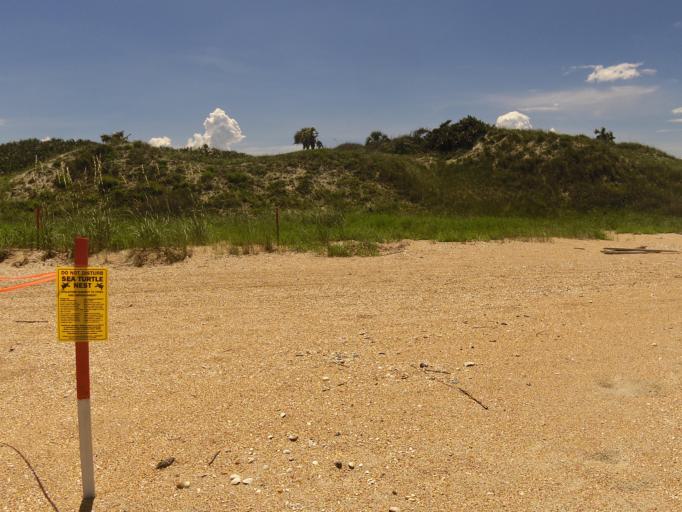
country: US
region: Florida
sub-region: Saint Johns County
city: Palm Valley
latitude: 30.1132
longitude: -81.3439
